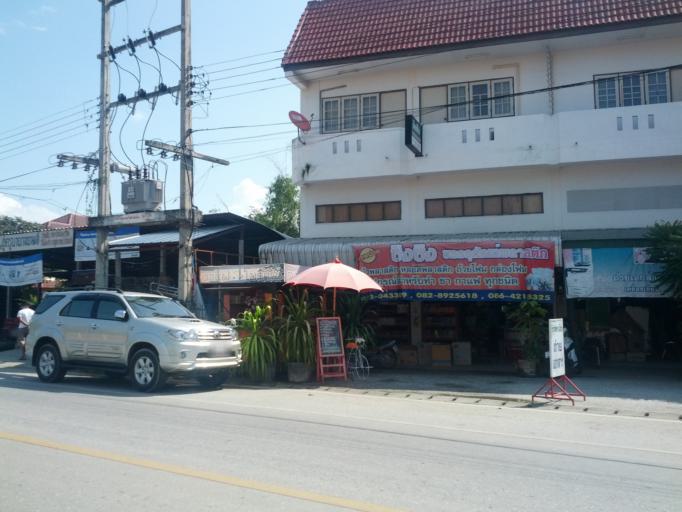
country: TH
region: Chiang Mai
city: San Kamphaeng
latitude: 18.7956
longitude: 99.1068
